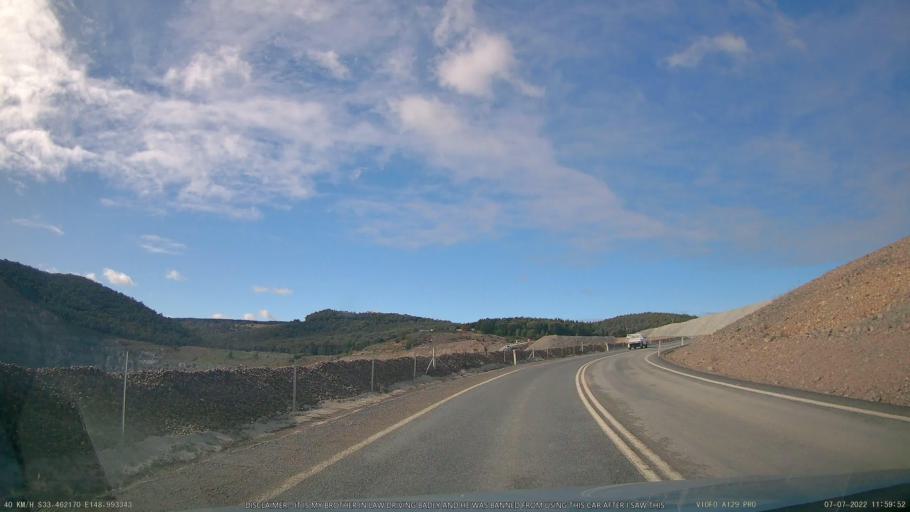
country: AU
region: New South Wales
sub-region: Blayney
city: Millthorpe
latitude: -33.4621
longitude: 148.9937
